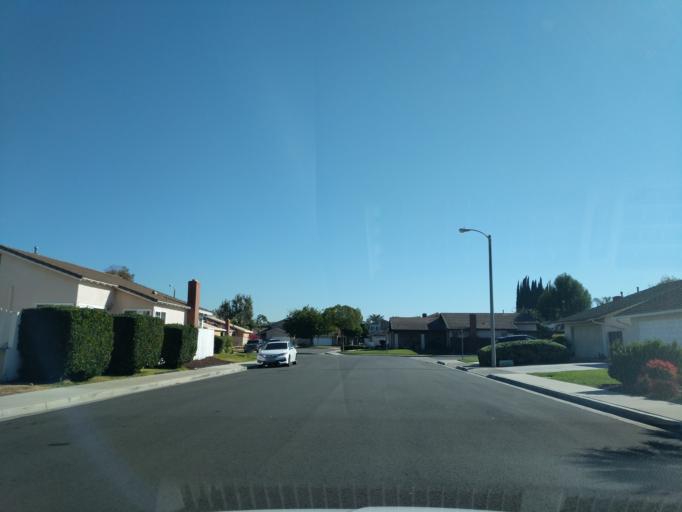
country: US
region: California
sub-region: Orange County
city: Irvine
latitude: 33.7077
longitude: -117.7896
